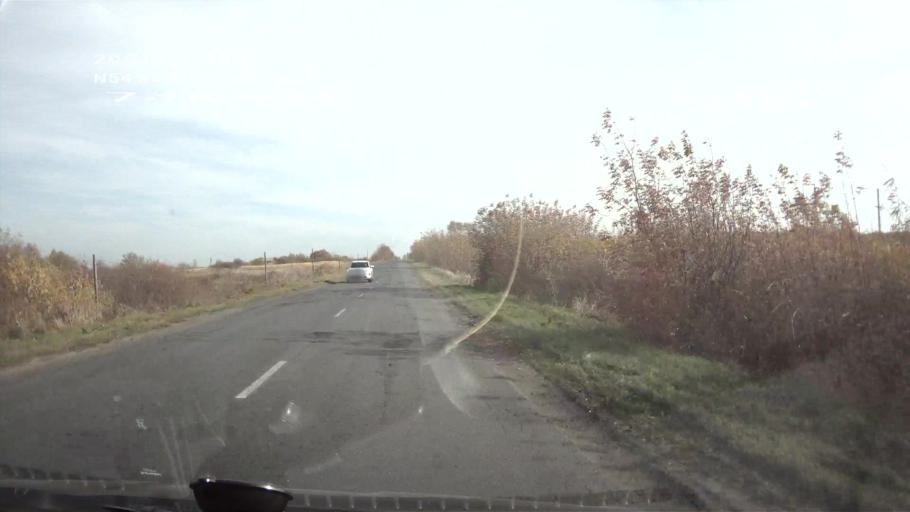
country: RU
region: Chuvashia
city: Alatyr'
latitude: 54.8452
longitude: 46.4602
